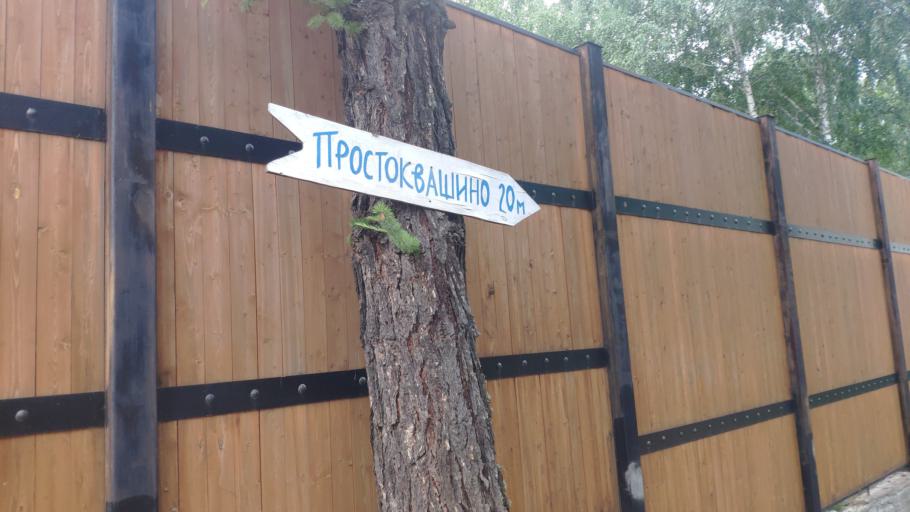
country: RU
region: Bashkortostan
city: Abzakovo
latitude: 53.8035
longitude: 58.6444
